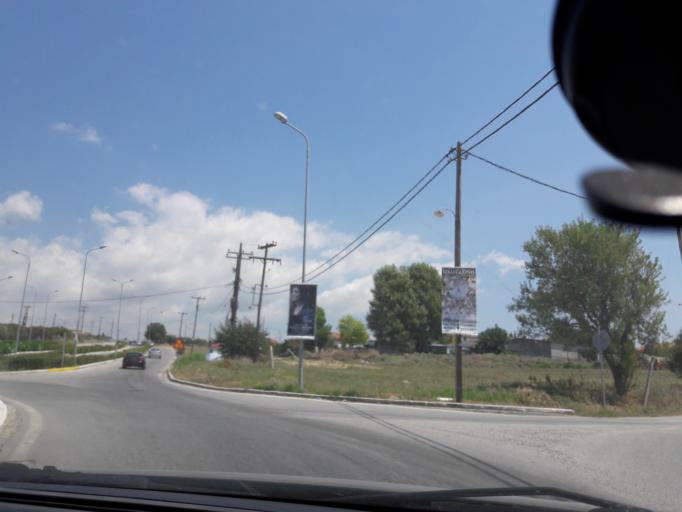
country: GR
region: Central Macedonia
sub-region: Nomos Chalkidikis
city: Nea Kallikrateia
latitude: 40.3156
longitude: 23.0675
